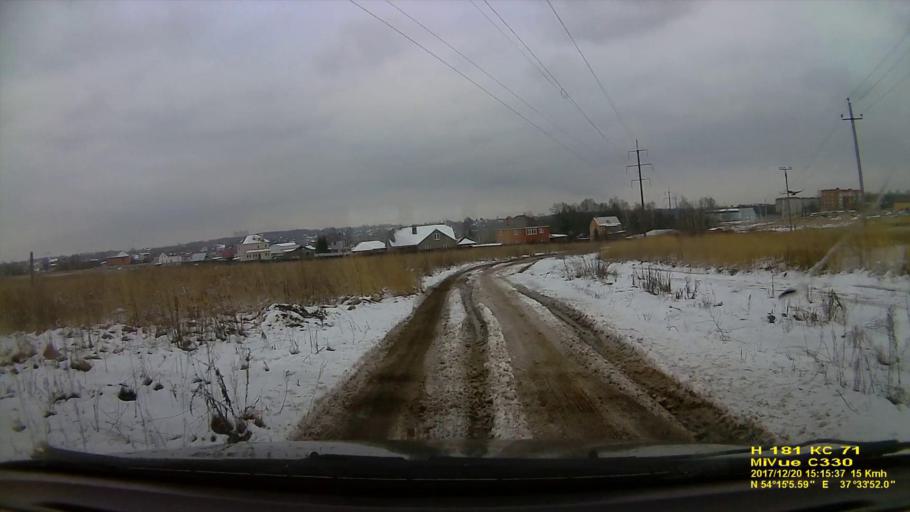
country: RU
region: Tula
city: Gorelki
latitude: 54.2515
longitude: 37.5645
